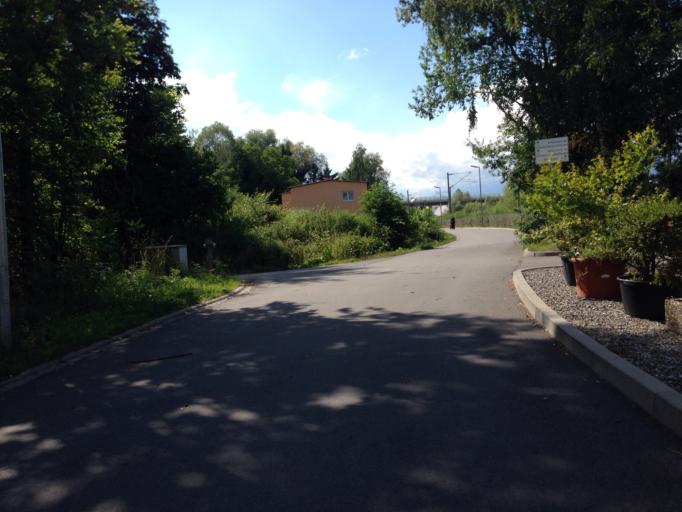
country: CH
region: Thurgau
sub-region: Kreuzlingen District
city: Gottlieben
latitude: 47.6862
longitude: 9.1352
